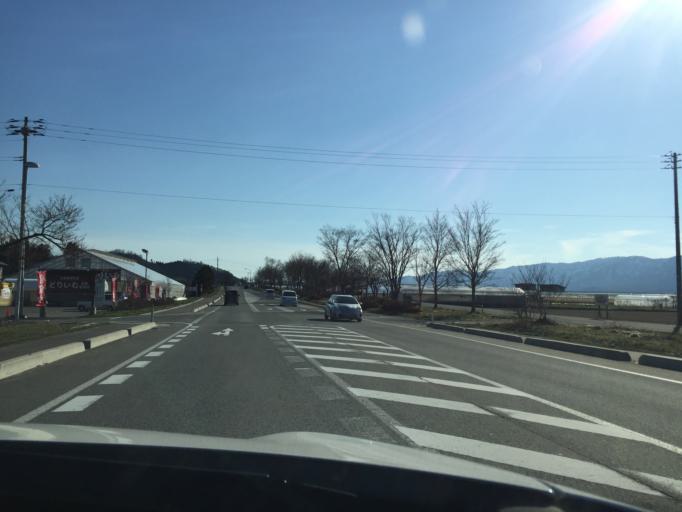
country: JP
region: Yamagata
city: Nagai
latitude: 38.1698
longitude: 140.0884
